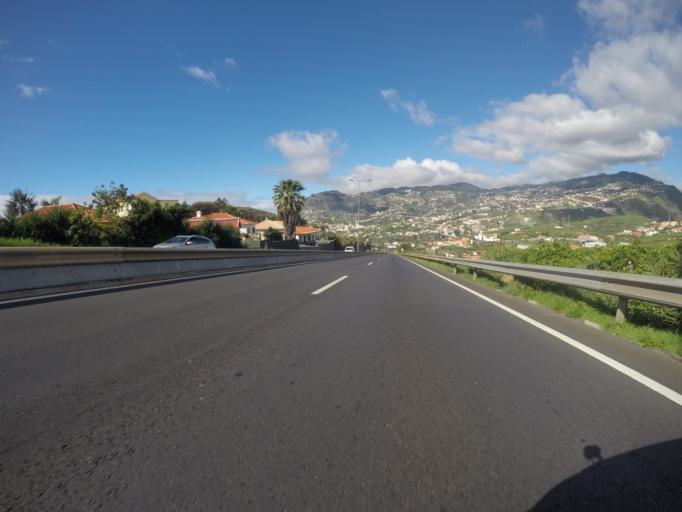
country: PT
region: Madeira
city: Camara de Lobos
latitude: 32.6479
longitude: -16.9544
